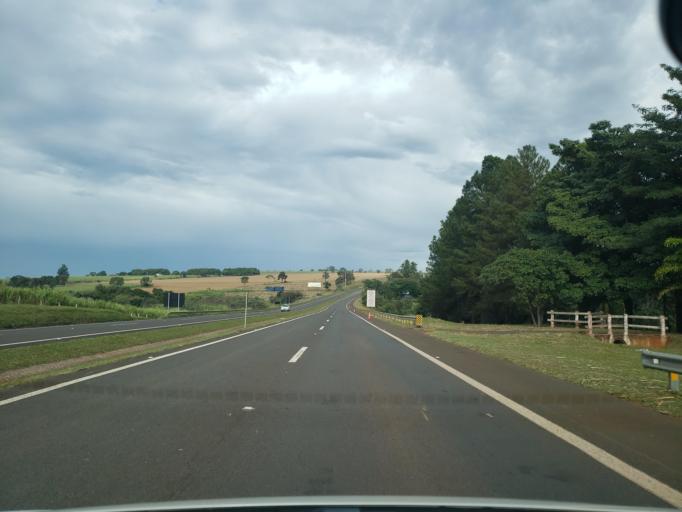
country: BR
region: Sao Paulo
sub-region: Dois Corregos
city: Dois Corregos
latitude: -22.2531
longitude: -48.3623
